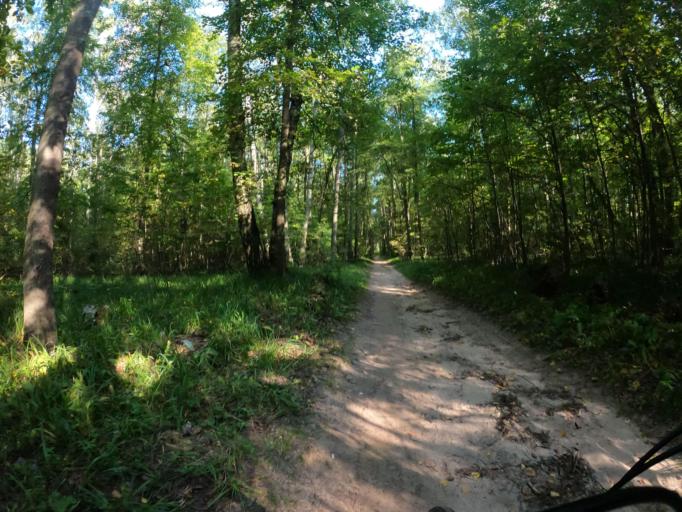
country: RU
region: Moskovskaya
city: Stupino
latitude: 54.8762
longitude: 38.0950
